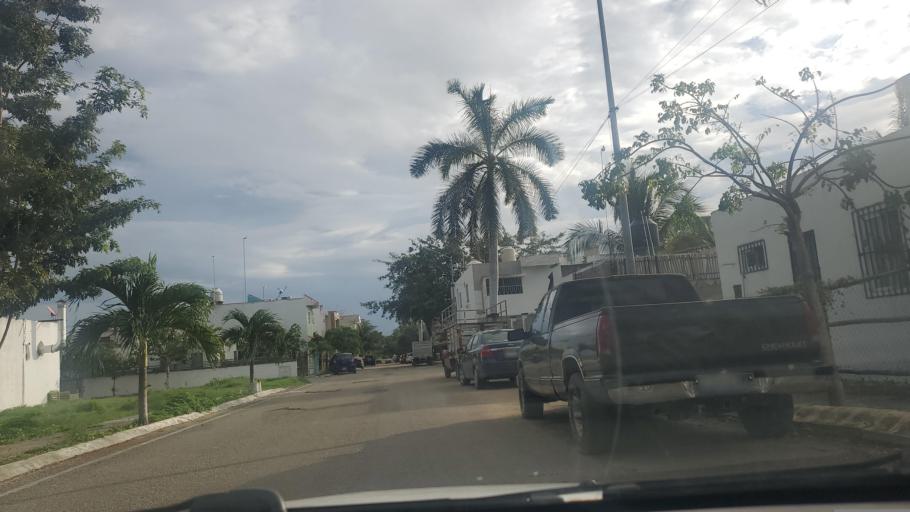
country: MX
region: Quintana Roo
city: Tulum
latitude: 20.2151
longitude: -87.4574
